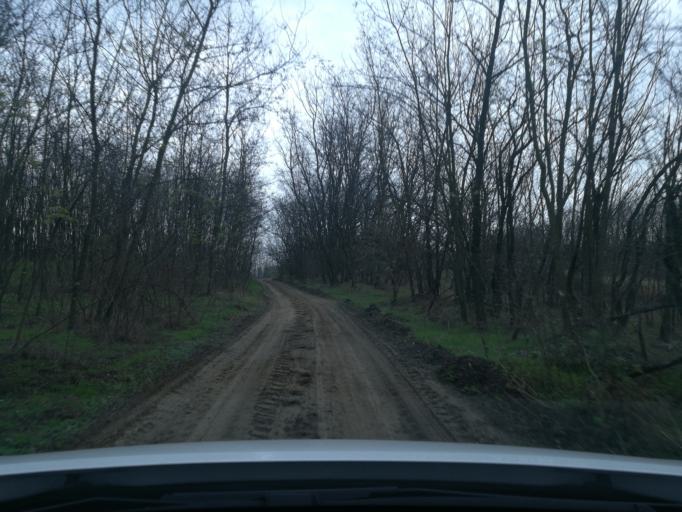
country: HU
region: Szabolcs-Szatmar-Bereg
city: Nyirpazony
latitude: 47.9700
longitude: 21.7896
